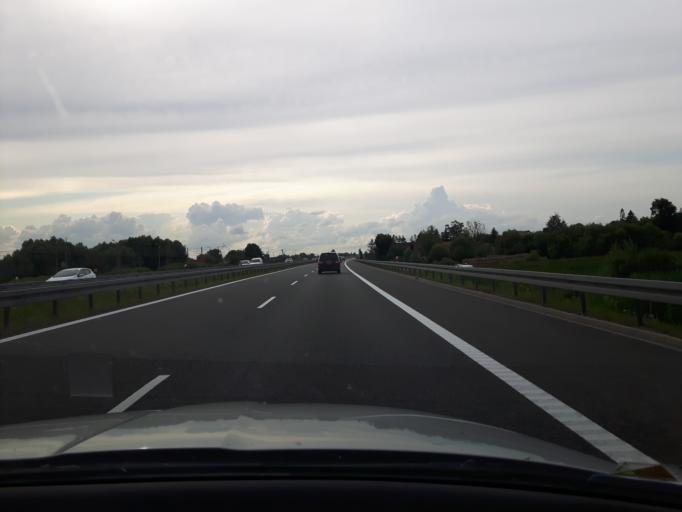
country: PL
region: Warmian-Masurian Voivodeship
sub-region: Powiat elblaski
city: Gronowo Gorne
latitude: 54.1044
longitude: 19.5145
